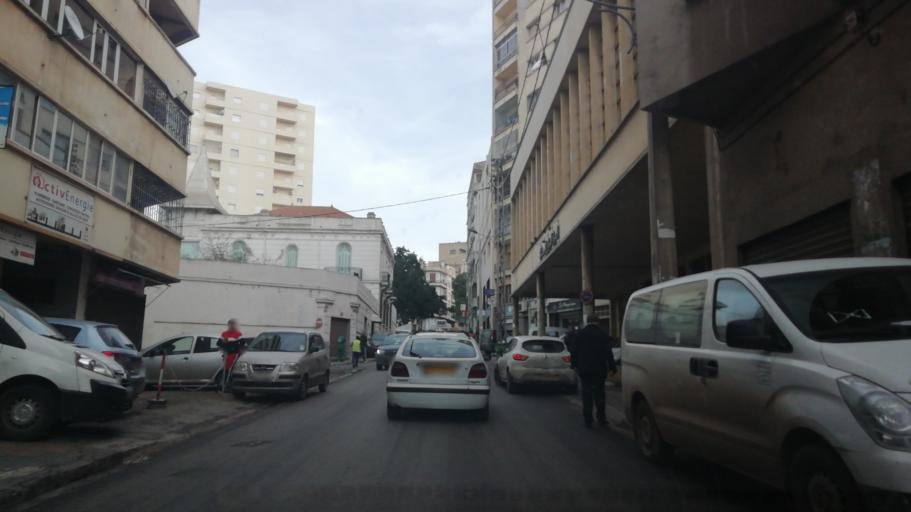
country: DZ
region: Oran
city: Oran
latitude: 35.7027
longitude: -0.6349
